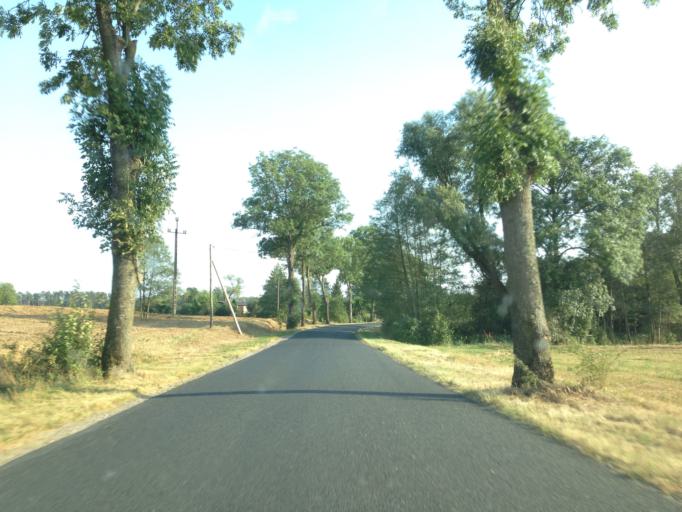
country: PL
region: Kujawsko-Pomorskie
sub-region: Powiat brodnicki
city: Brodnica
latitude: 53.3726
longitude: 19.3741
